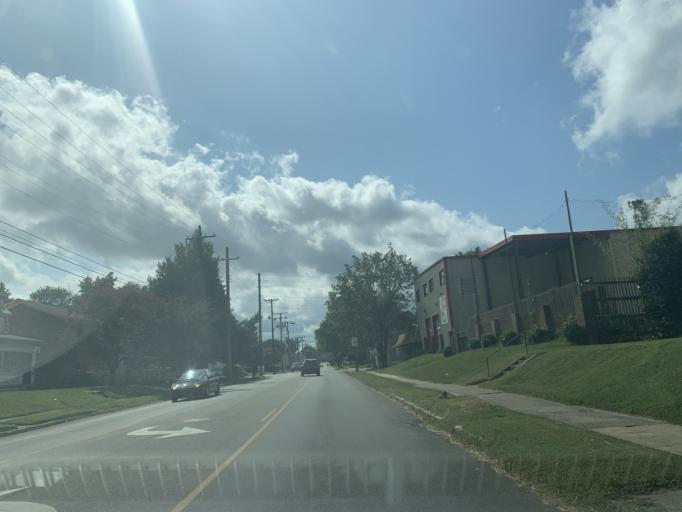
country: US
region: Kentucky
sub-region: Jefferson County
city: Audubon Park
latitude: 38.1975
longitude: -85.7651
